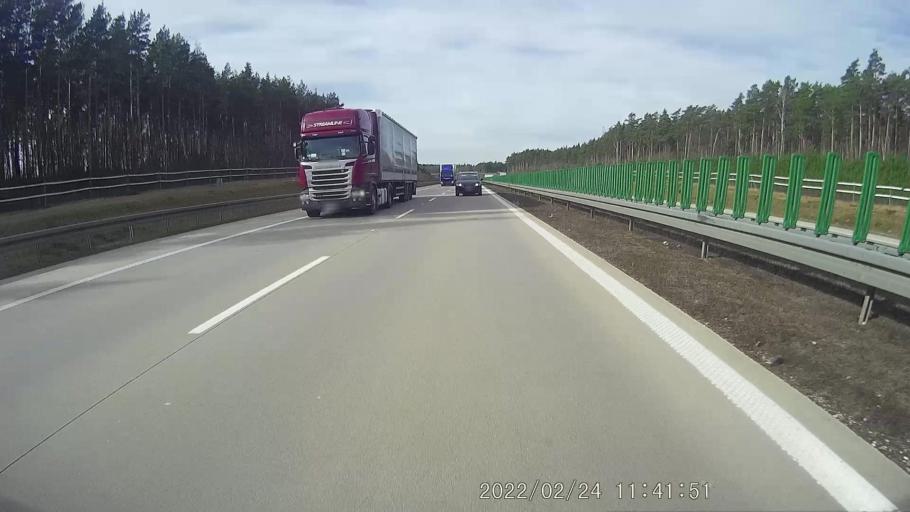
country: PL
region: Lower Silesian Voivodeship
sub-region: Powiat polkowicki
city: Radwanice
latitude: 51.5475
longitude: 15.8997
